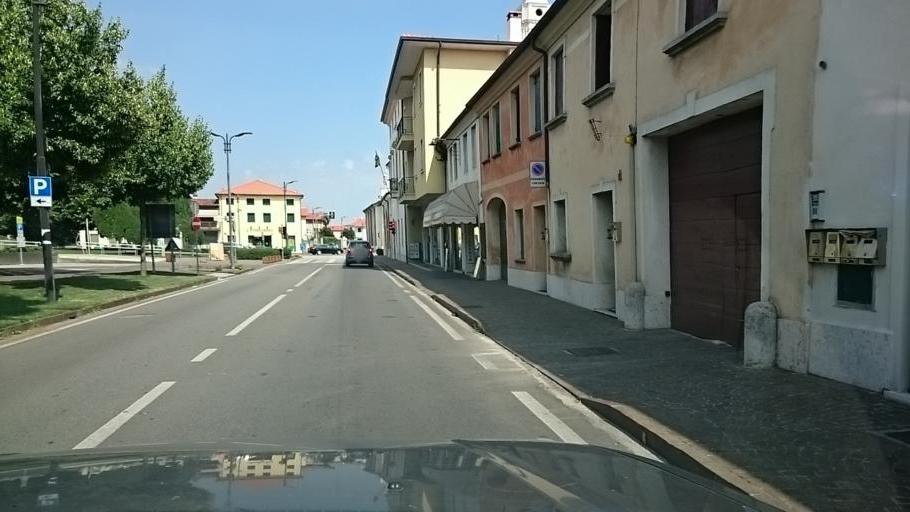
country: IT
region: Veneto
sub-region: Provincia di Vicenza
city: Rosa
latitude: 45.7243
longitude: 11.7615
